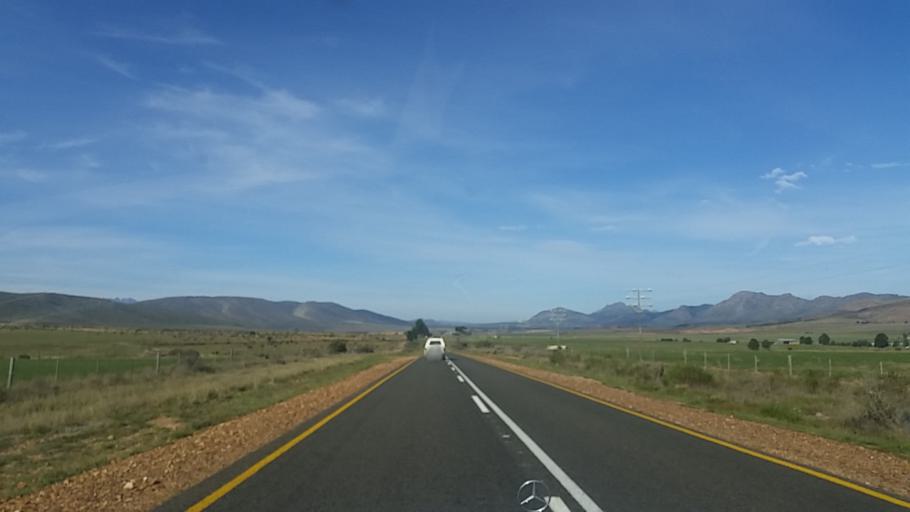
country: ZA
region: Western Cape
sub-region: Eden District Municipality
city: George
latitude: -33.8194
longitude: 22.4991
